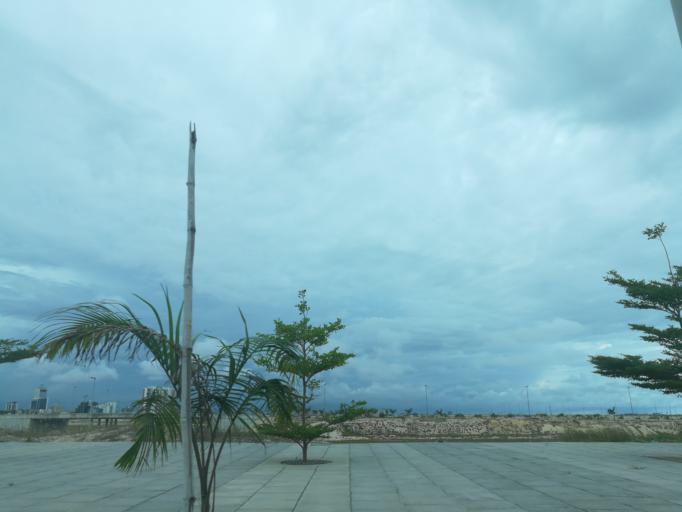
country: NG
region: Lagos
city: Ikoyi
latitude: 6.4126
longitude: 3.4166
